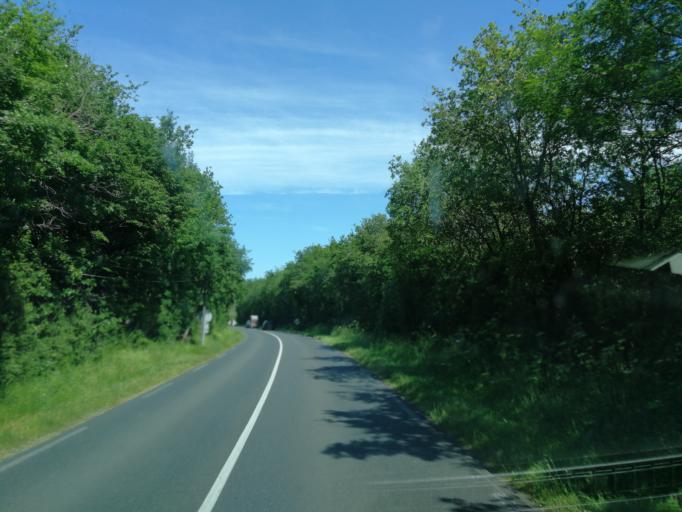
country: FR
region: Poitou-Charentes
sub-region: Departement des Deux-Sevres
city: Saint-Leger-de-Montbrun
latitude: 46.9735
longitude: -0.0990
